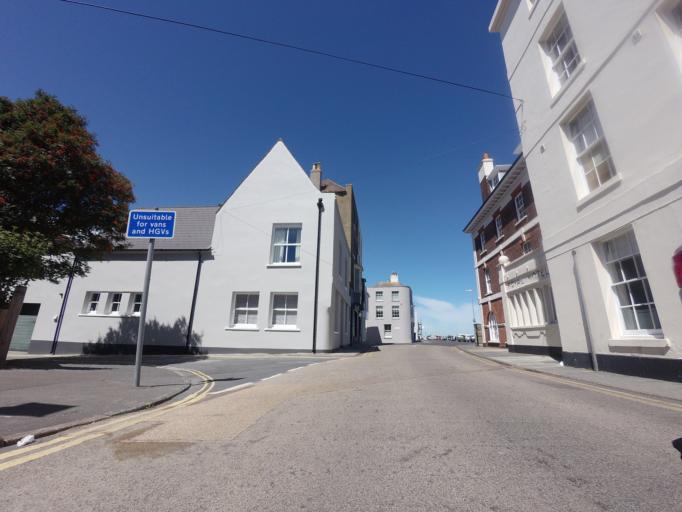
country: GB
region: England
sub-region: Kent
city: Deal
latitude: 51.2253
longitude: 1.4042
